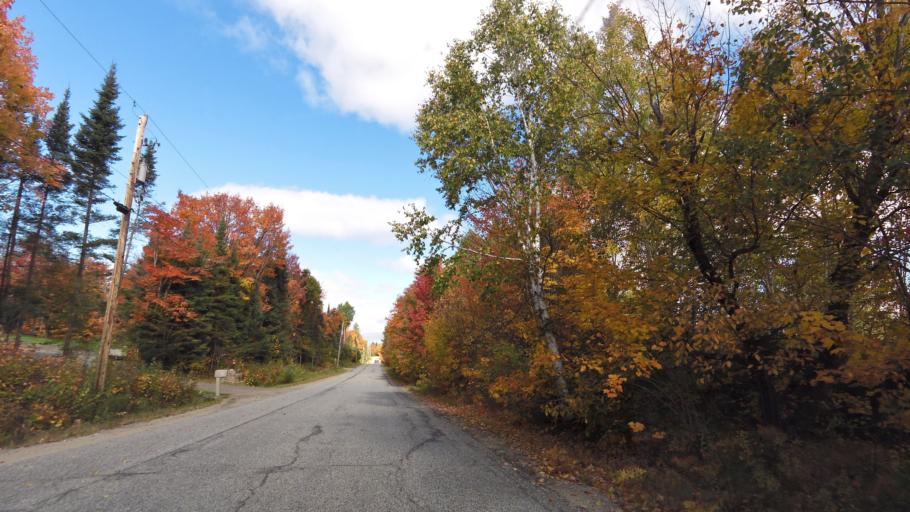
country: CA
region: Ontario
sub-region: Nipissing District
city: North Bay
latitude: 46.3715
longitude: -79.4871
